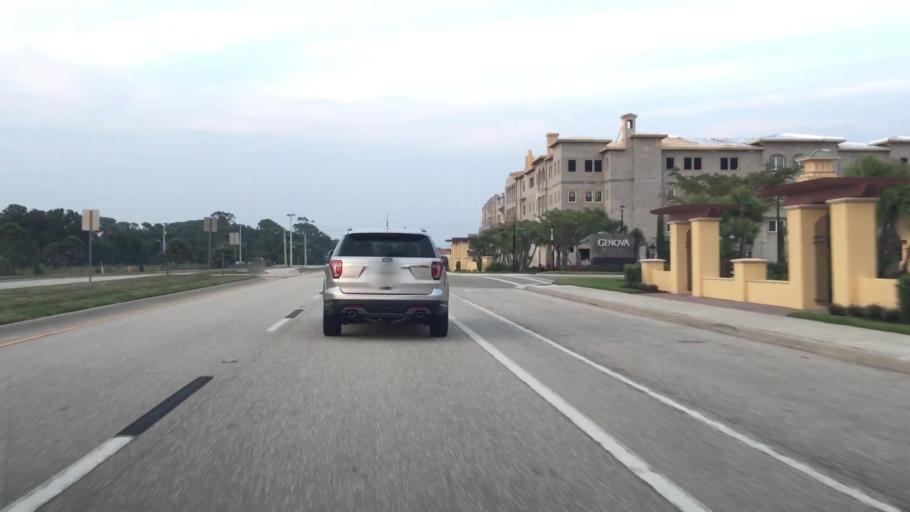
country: US
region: Florida
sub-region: Lee County
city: Estero
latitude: 26.4286
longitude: -81.8047
